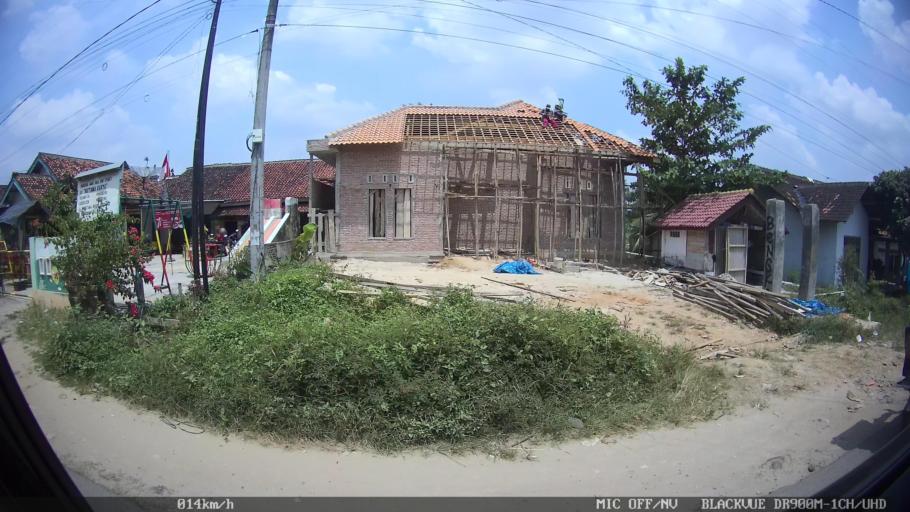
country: ID
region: Lampung
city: Pringsewu
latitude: -5.3462
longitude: 104.9862
